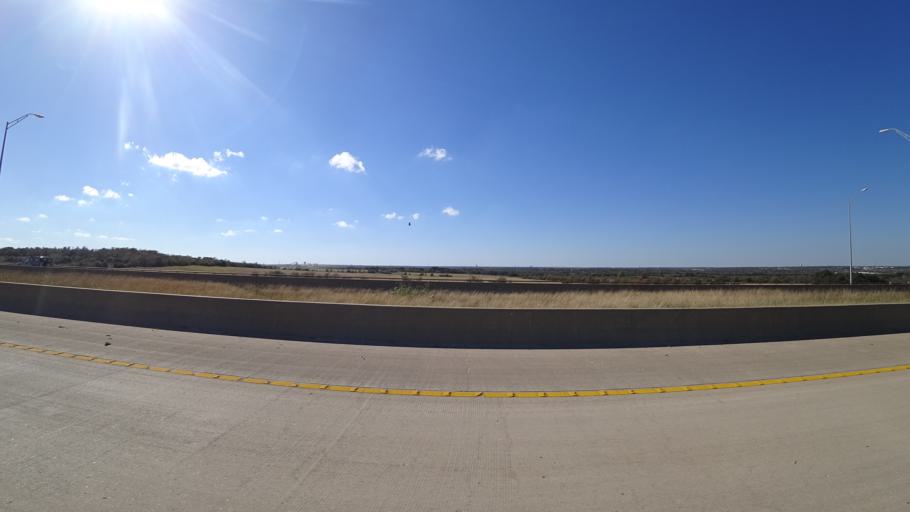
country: US
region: Texas
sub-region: Travis County
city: Wells Branch
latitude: 30.4668
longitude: -97.7012
